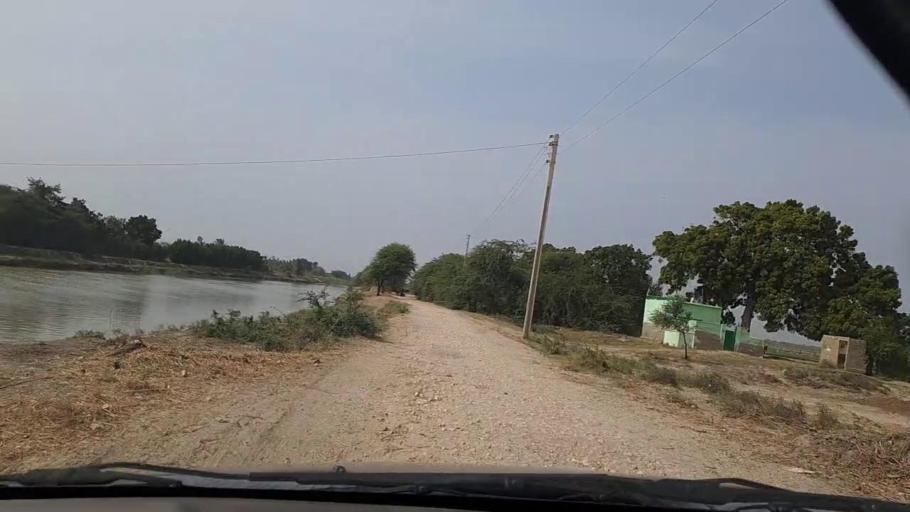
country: PK
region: Sindh
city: Thatta
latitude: 24.5705
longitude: 67.8569
